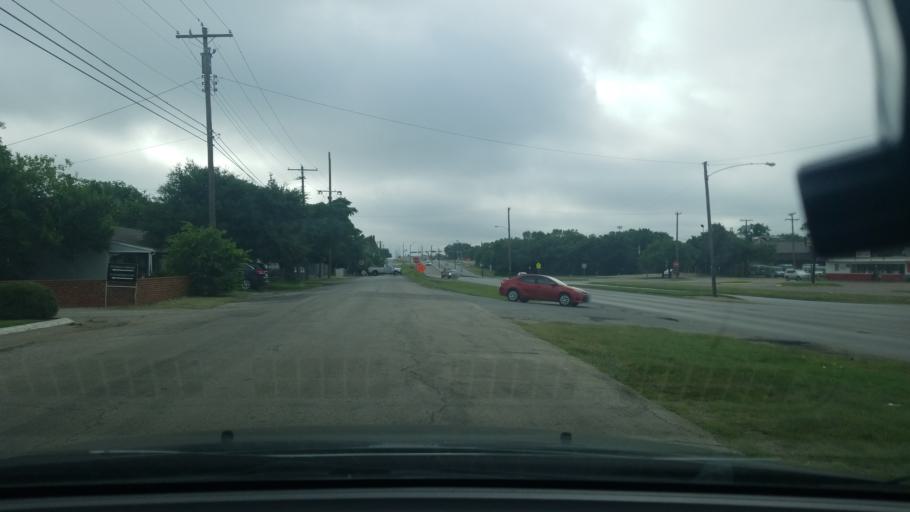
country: US
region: Texas
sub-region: Dallas County
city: Balch Springs
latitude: 32.7712
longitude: -96.6907
